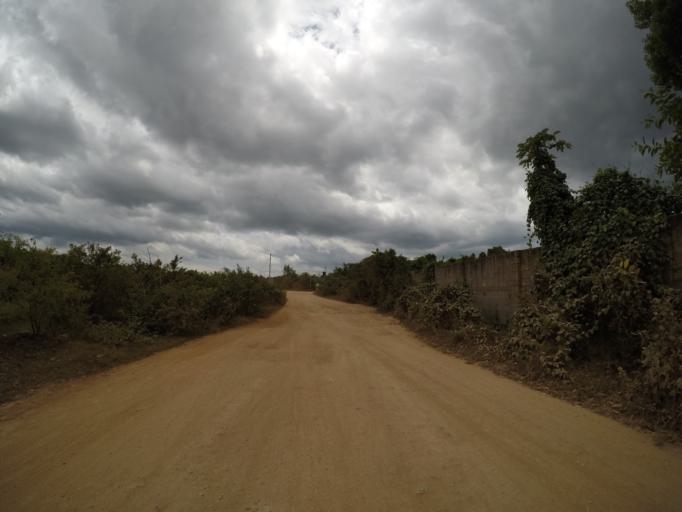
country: TZ
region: Zanzibar Central/South
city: Koani
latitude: -6.1974
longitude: 39.3093
